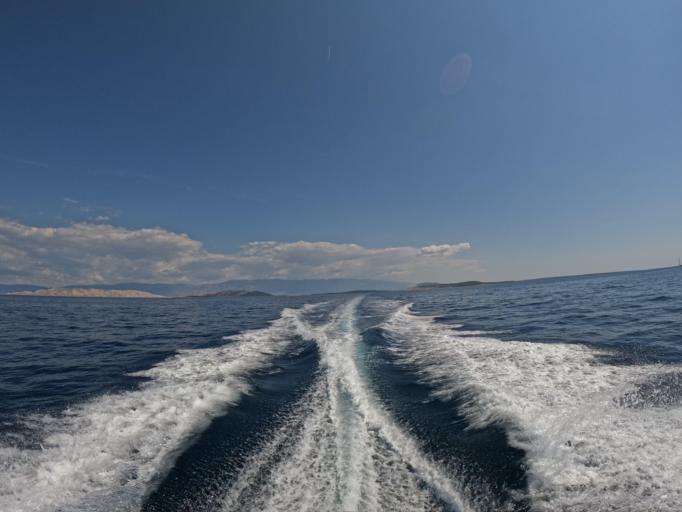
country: HR
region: Primorsko-Goranska
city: Lopar
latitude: 44.8839
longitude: 14.6451
